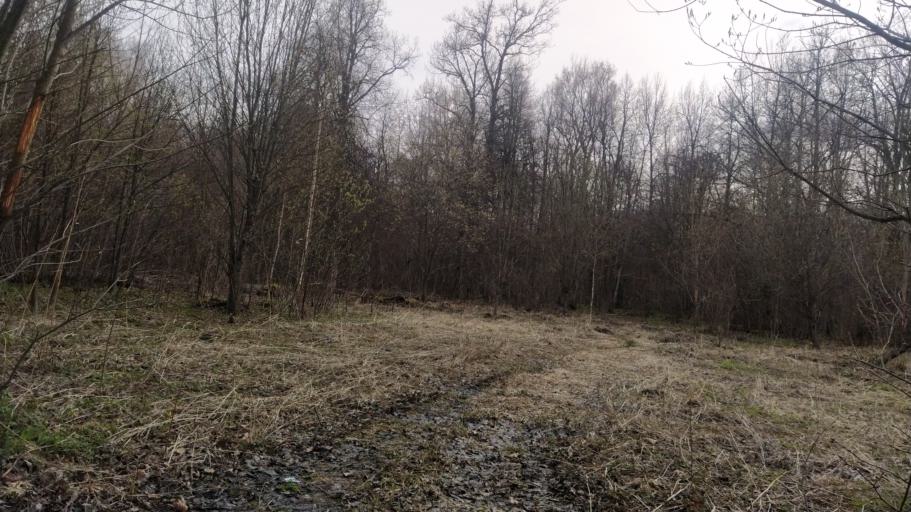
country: RU
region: Chuvashia
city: Novyye Lapsary
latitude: 56.1393
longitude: 47.1235
